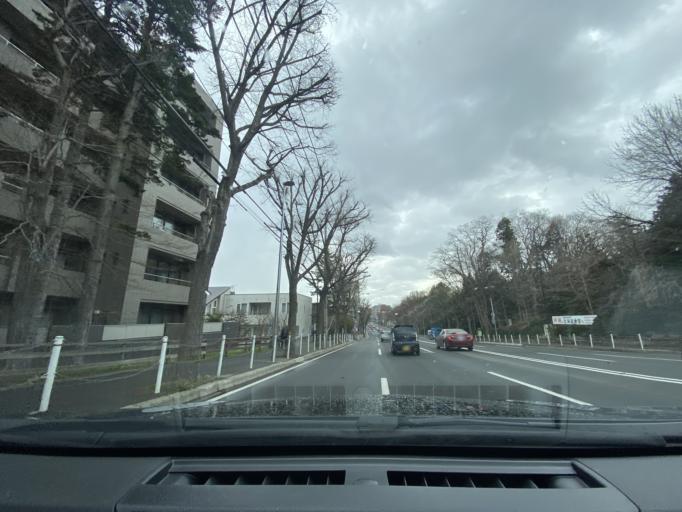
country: JP
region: Hokkaido
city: Sapporo
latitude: 43.0570
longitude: 141.3101
